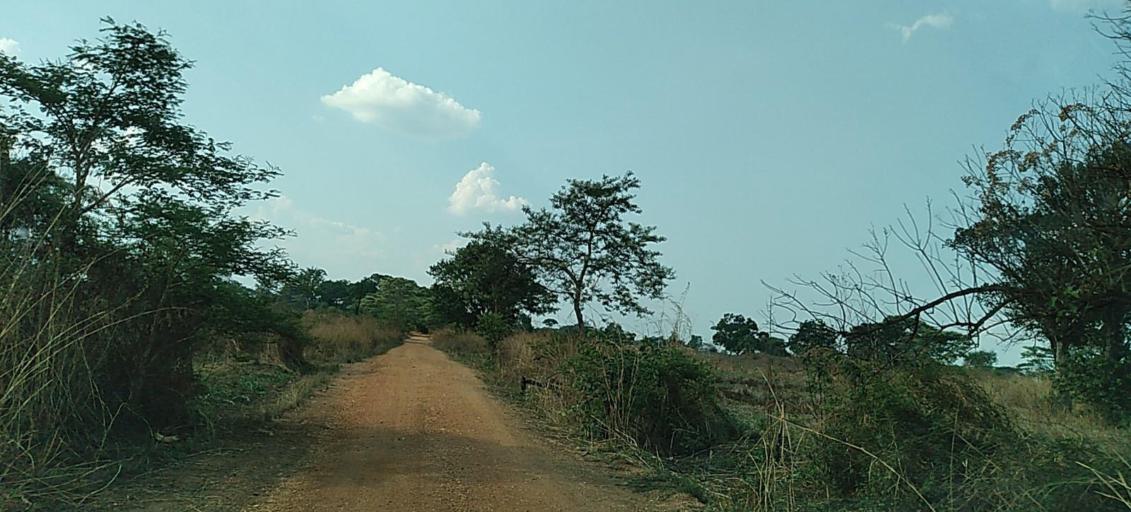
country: ZM
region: Copperbelt
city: Mpongwe
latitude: -13.4978
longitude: 28.0875
